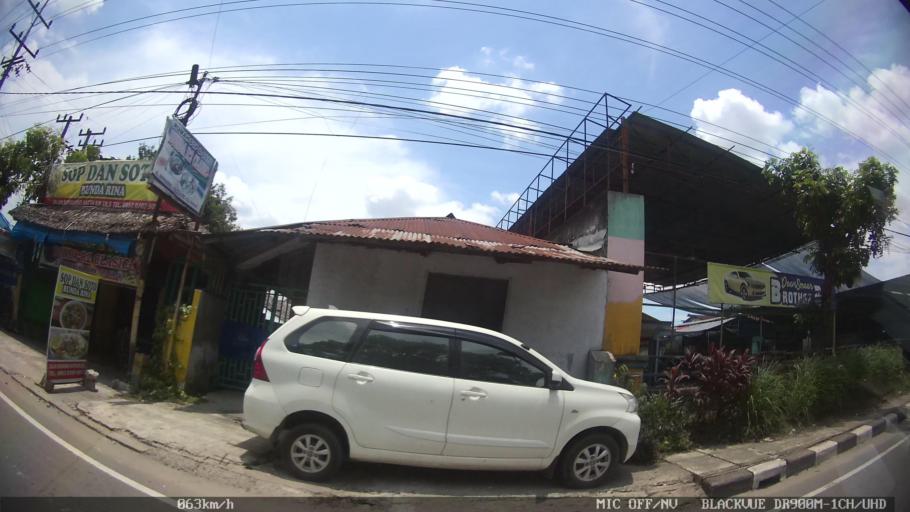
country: ID
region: North Sumatra
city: Binjai
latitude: 3.6071
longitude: 98.5228
